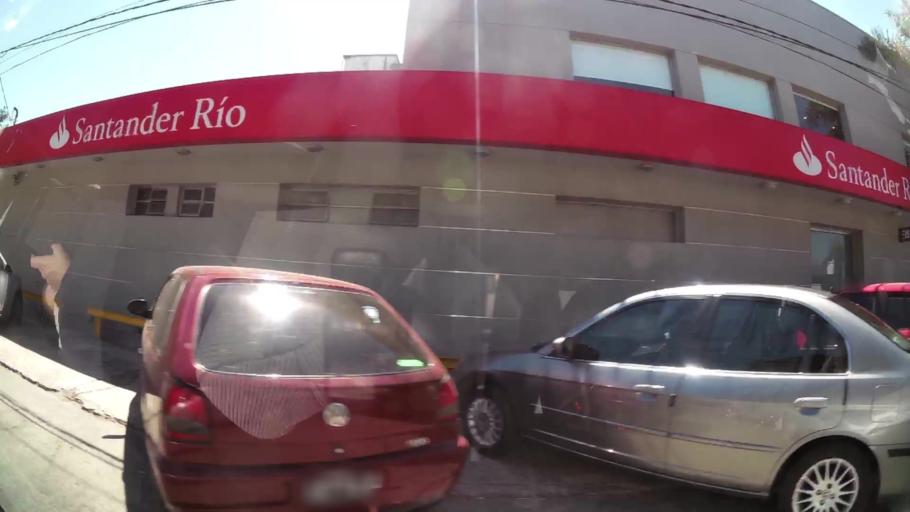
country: AR
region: Buenos Aires
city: Hurlingham
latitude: -34.4997
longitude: -58.6424
